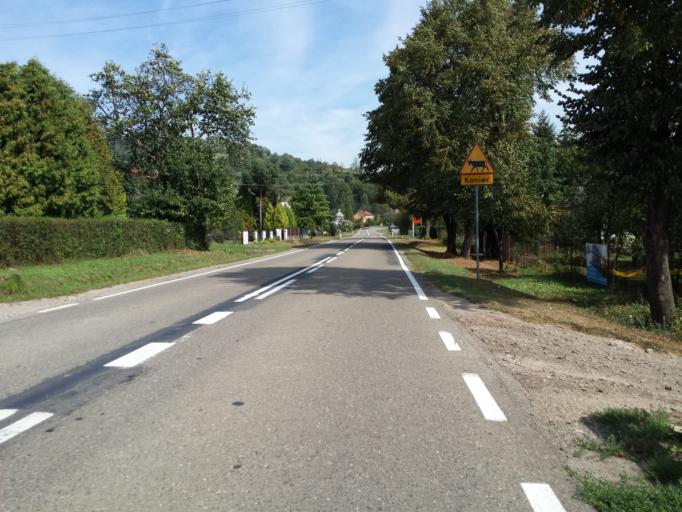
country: PL
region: Subcarpathian Voivodeship
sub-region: Powiat leski
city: Baligrod
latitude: 49.4029
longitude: 22.2886
